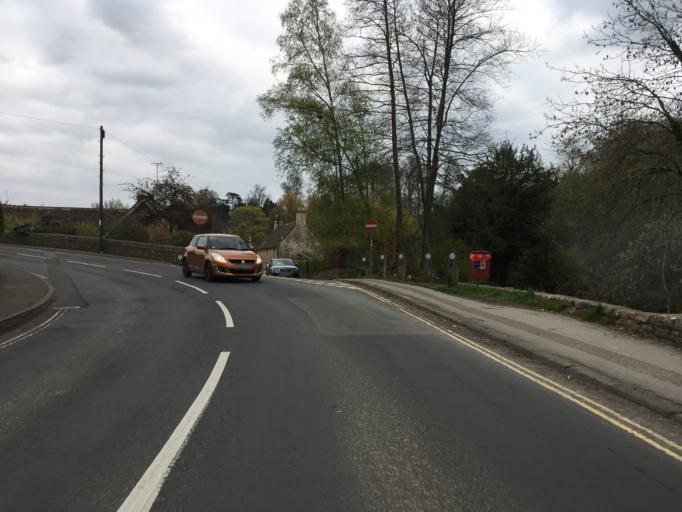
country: GB
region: England
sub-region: Gloucestershire
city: Northleach
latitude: 51.7582
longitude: -1.8331
